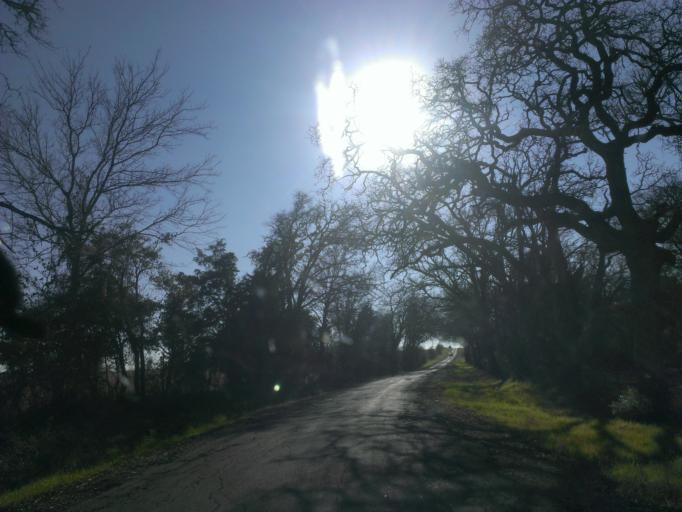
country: US
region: Texas
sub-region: Milam County
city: Thorndale
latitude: 30.4861
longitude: -97.2379
